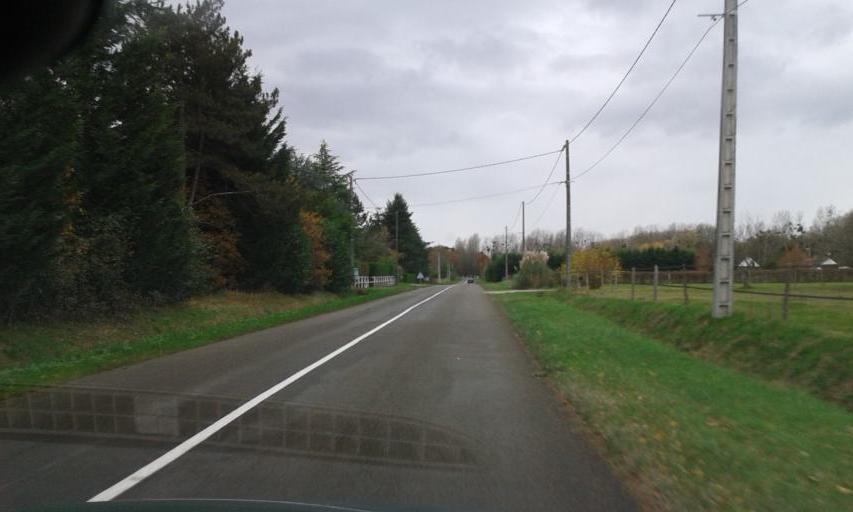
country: FR
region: Centre
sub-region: Departement du Loiret
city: Vitry-aux-Loges
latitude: 47.9322
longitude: 2.2434
